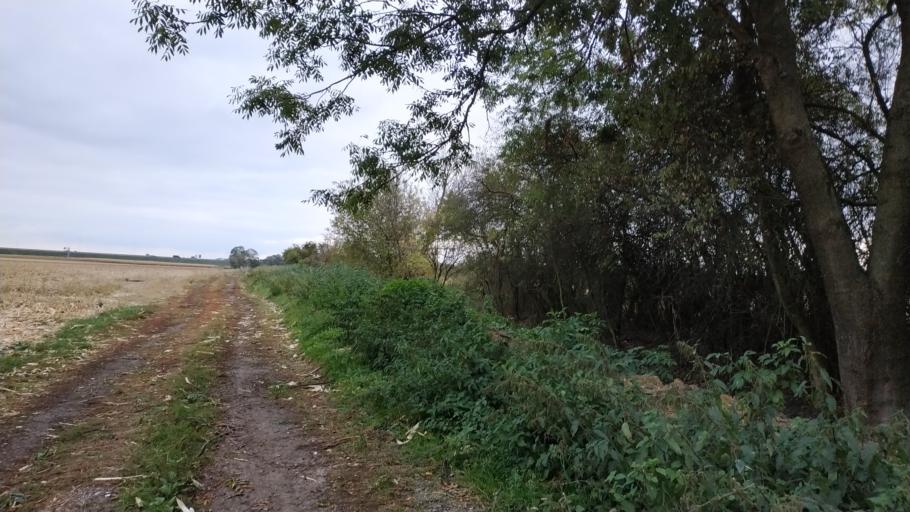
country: PL
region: Lower Silesian Voivodeship
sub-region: Powiat wroclawski
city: Tyniec Maly
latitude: 51.0262
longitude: 16.9318
